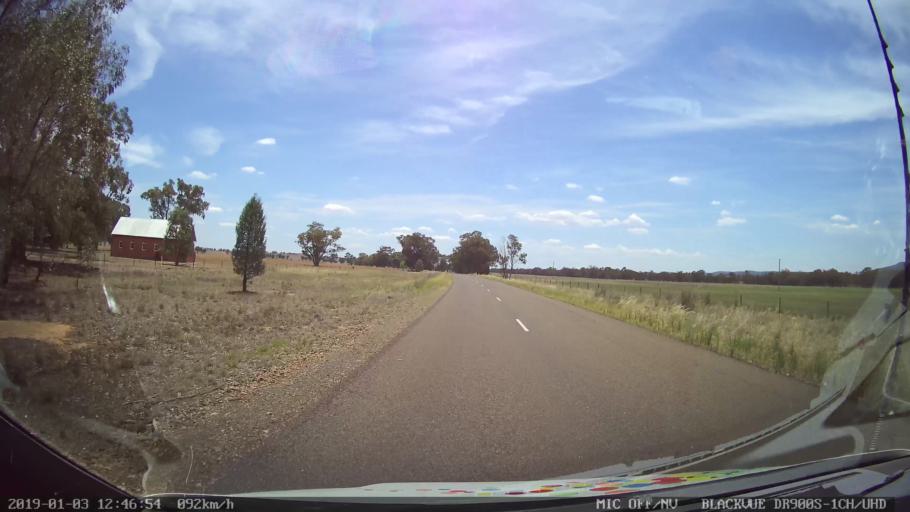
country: AU
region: New South Wales
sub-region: Weddin
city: Grenfell
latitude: -33.7341
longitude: 148.2391
